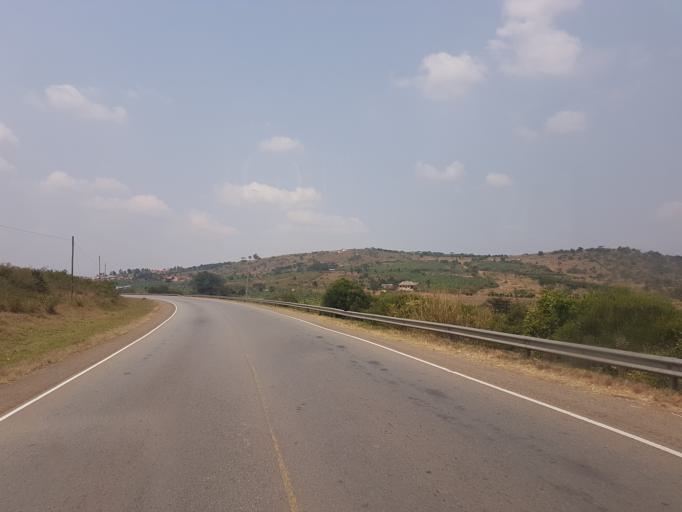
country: UG
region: Western Region
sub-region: Mbarara District
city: Mbarara
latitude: -0.5036
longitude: 30.8947
